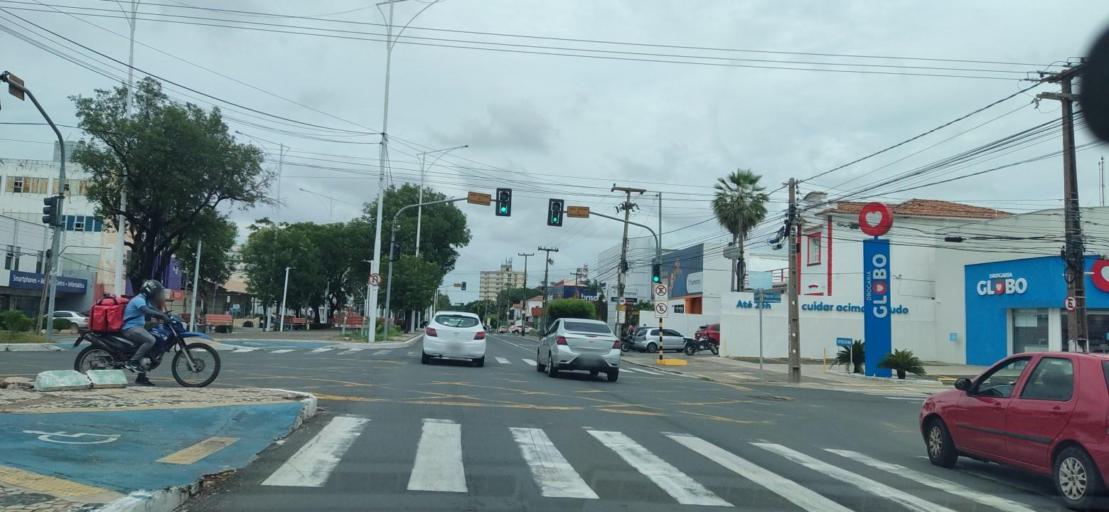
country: BR
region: Piaui
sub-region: Teresina
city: Teresina
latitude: -5.0877
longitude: -42.8056
